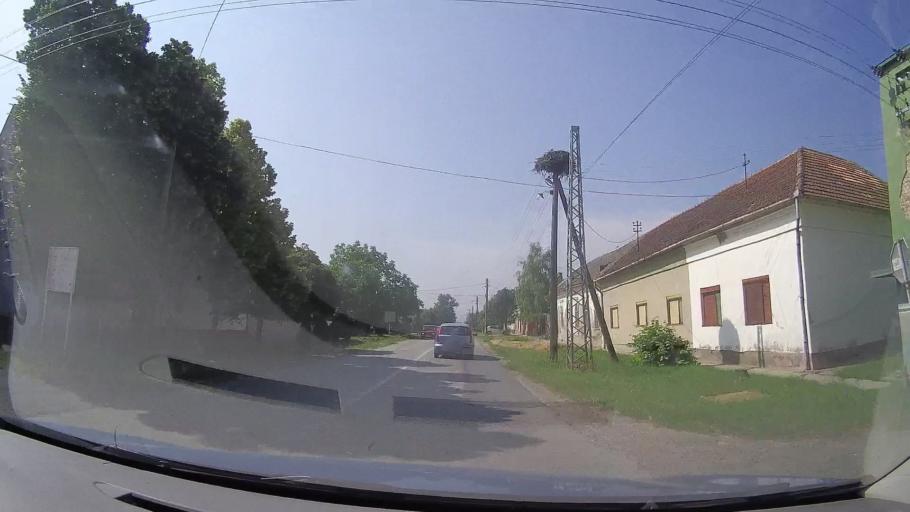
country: RS
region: Autonomna Pokrajina Vojvodina
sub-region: Srednjebanatski Okrug
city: Secanj
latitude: 45.3637
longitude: 20.7719
